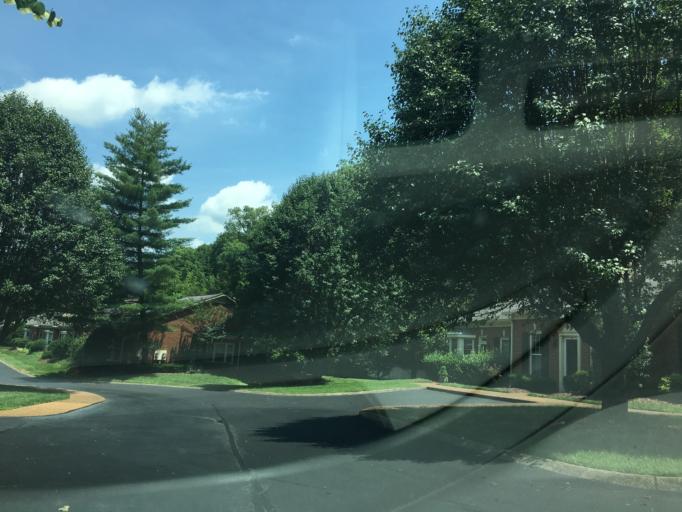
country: US
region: Tennessee
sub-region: Davidson County
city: Belle Meade
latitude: 36.0746
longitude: -86.9101
